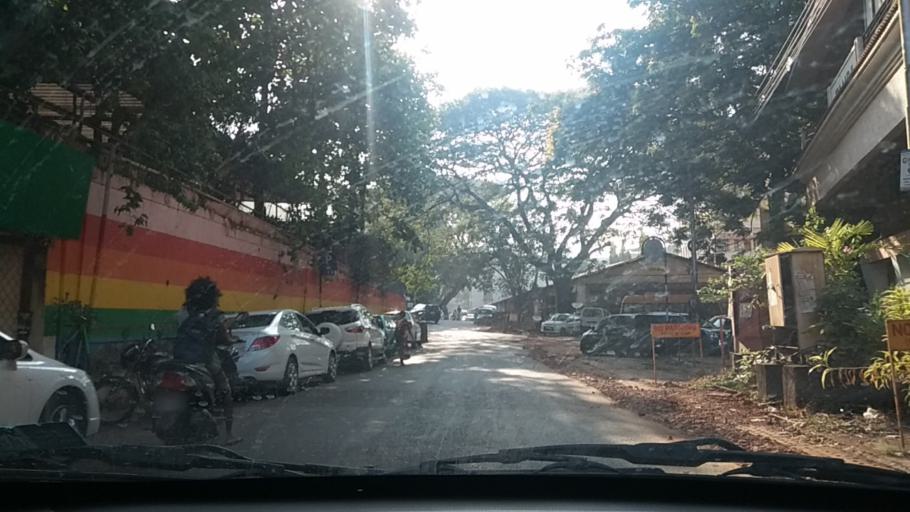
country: IN
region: Goa
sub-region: North Goa
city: Panaji
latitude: 15.4954
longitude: 73.8232
